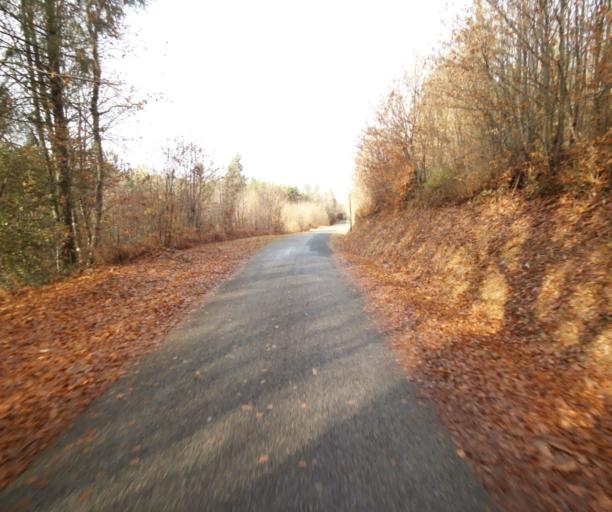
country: FR
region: Limousin
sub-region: Departement de la Correze
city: Sainte-Fortunade
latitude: 45.1978
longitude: 1.7337
